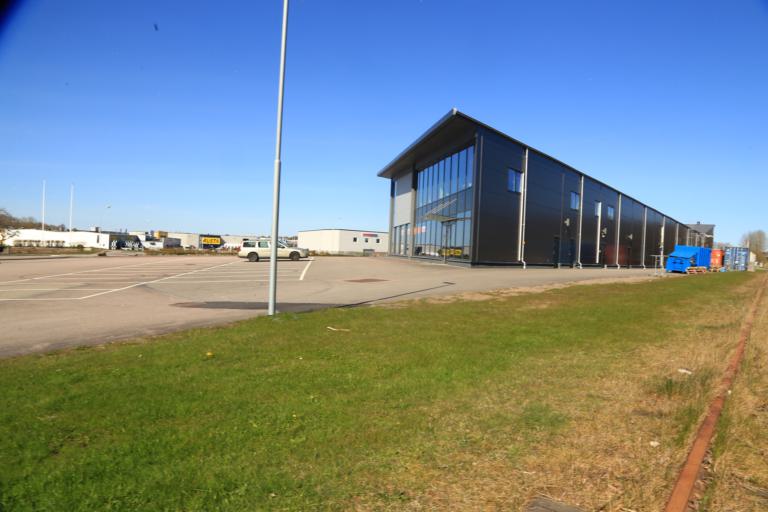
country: SE
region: Halland
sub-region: Varbergs Kommun
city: Varberg
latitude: 57.1200
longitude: 12.2585
